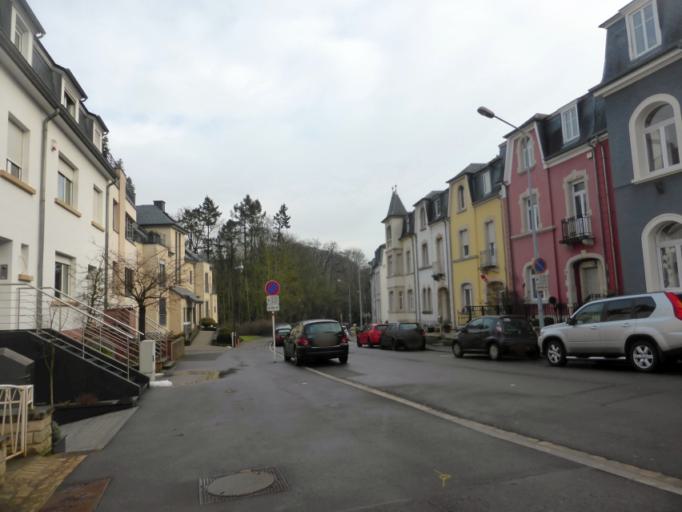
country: LU
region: Luxembourg
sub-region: Canton de Luxembourg
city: Luxembourg
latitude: 49.6083
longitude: 6.1433
